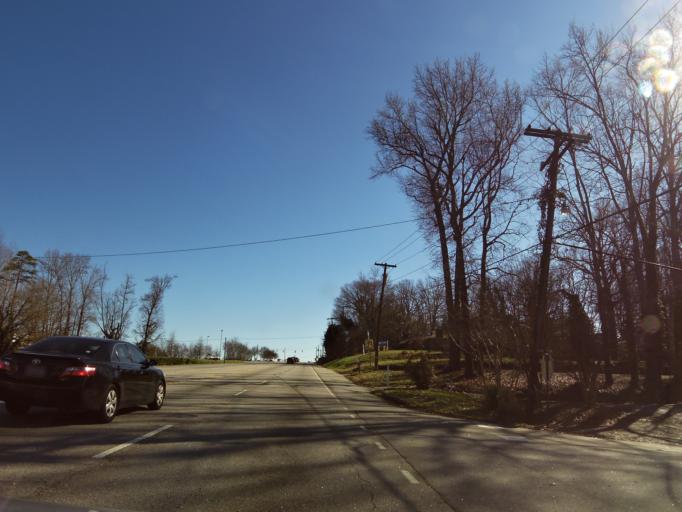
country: US
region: South Carolina
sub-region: Greenville County
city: Sans Souci
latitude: 34.8947
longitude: -82.4099
